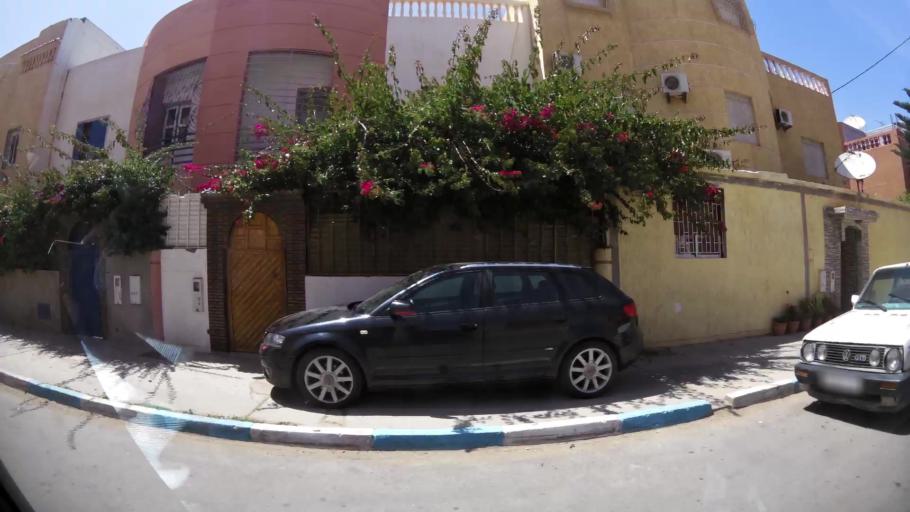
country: MA
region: Souss-Massa-Draa
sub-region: Inezgane-Ait Mellou
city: Inezgane
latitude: 30.3516
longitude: -9.4895
